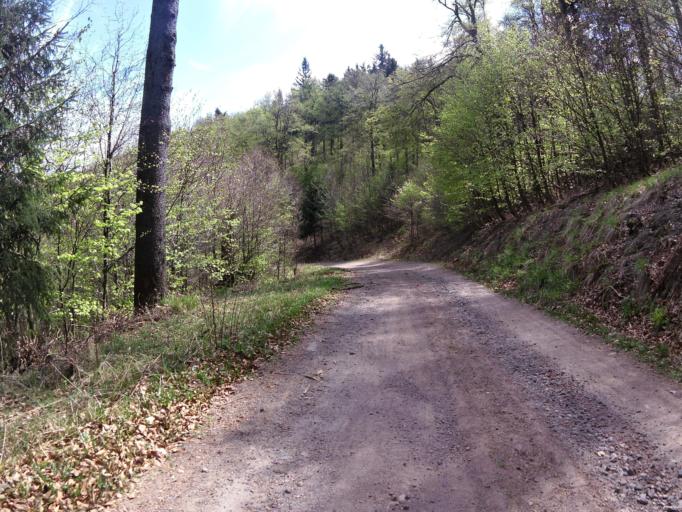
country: DE
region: Thuringia
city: Tabarz
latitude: 50.8385
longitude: 10.4939
